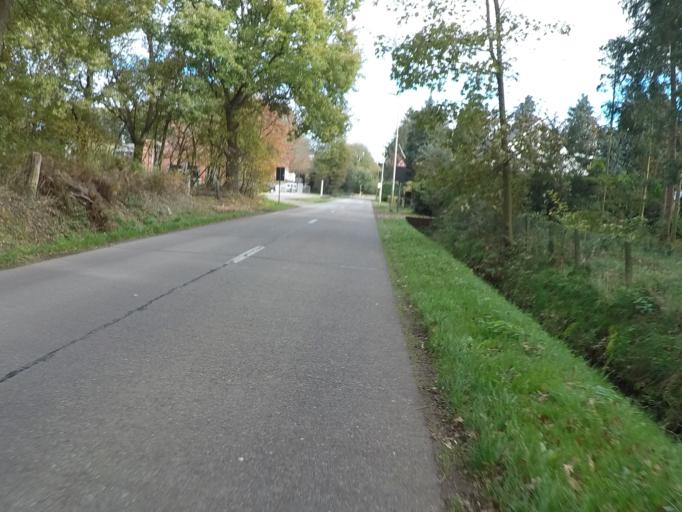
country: BE
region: Flanders
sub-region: Provincie Antwerpen
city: Berlaar
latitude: 51.1438
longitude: 4.6473
